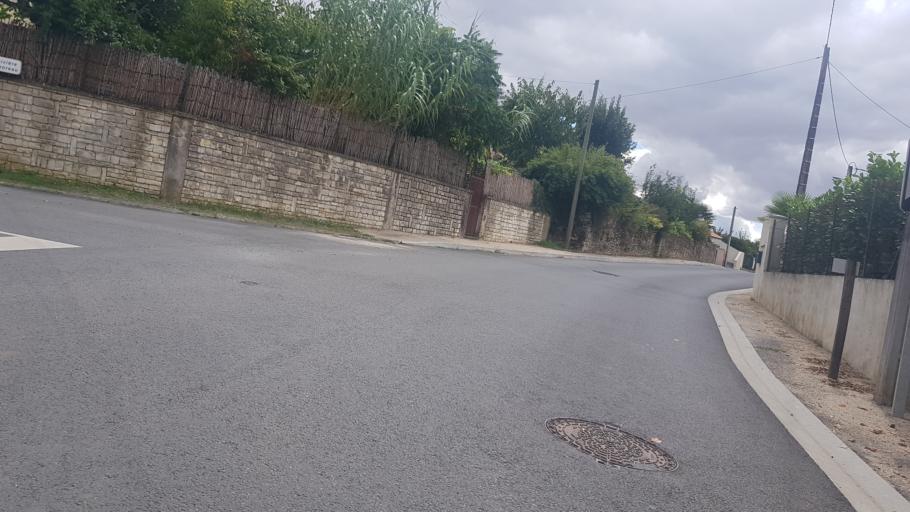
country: FR
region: Poitou-Charentes
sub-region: Departement des Deux-Sevres
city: Vouille
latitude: 46.3290
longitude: -0.3547
